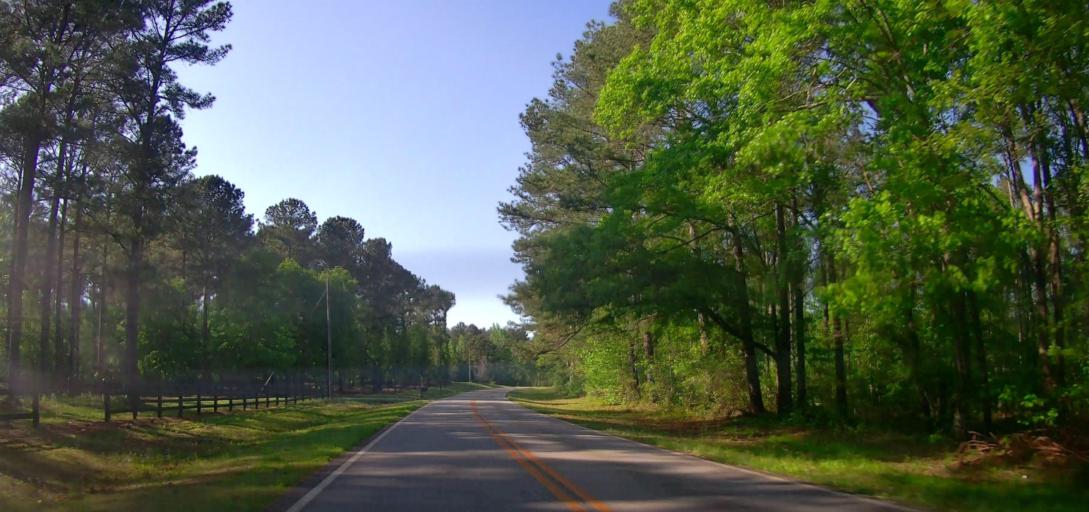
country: US
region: Georgia
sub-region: Morgan County
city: Madison
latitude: 33.5223
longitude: -83.5075
